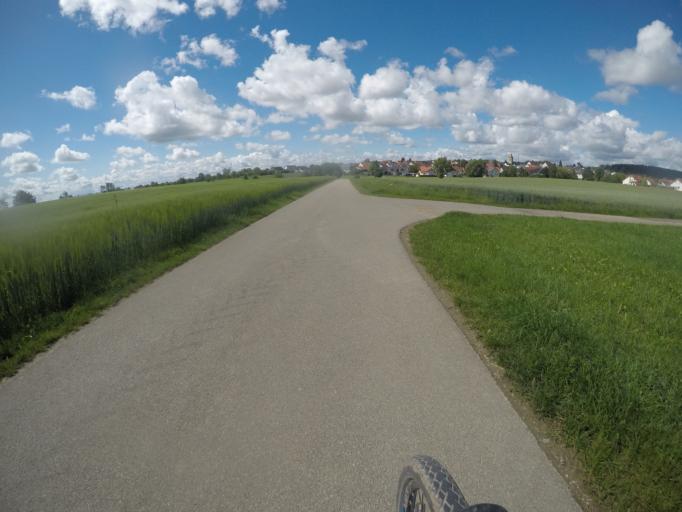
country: DE
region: Baden-Wuerttemberg
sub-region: Regierungsbezirk Stuttgart
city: Unterjettingen
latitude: 48.5704
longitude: 8.7879
